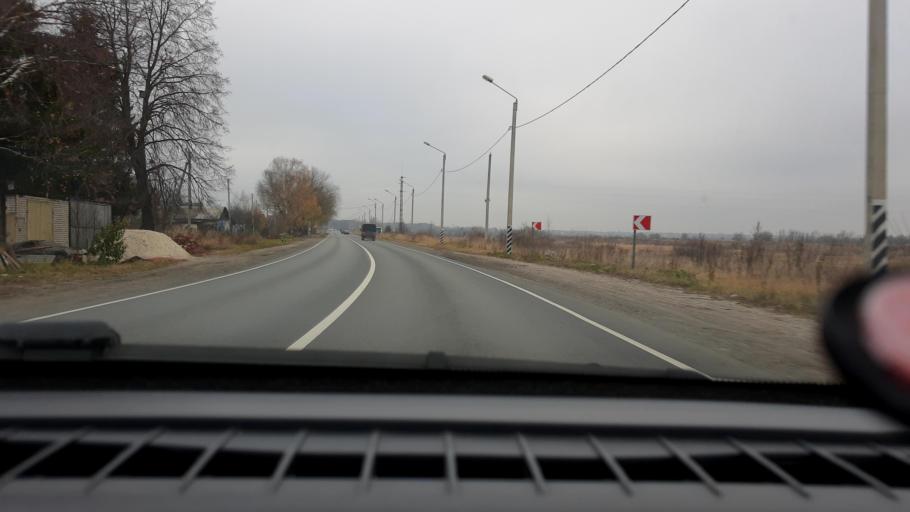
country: RU
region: Nizjnij Novgorod
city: Gidrotorf
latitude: 56.5528
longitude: 43.5182
